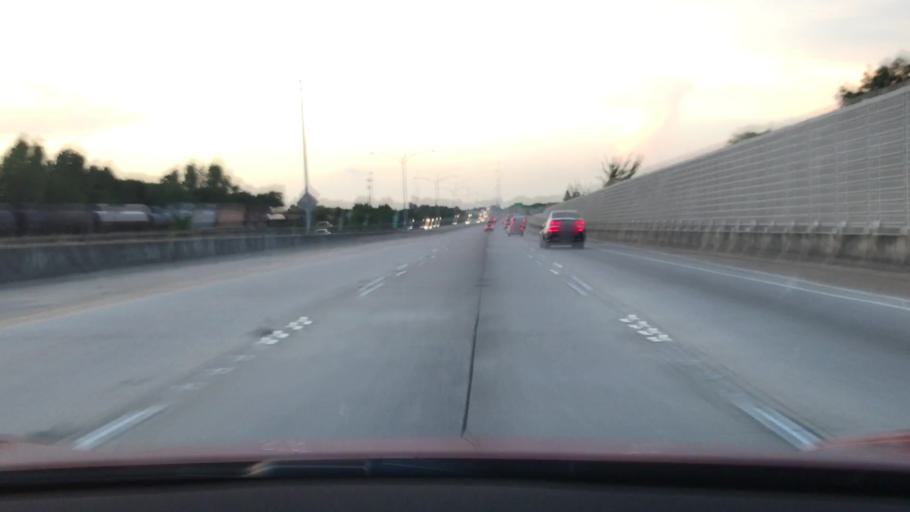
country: US
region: Louisiana
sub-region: Bossier Parish
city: Bossier City
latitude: 32.4703
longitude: -93.7552
